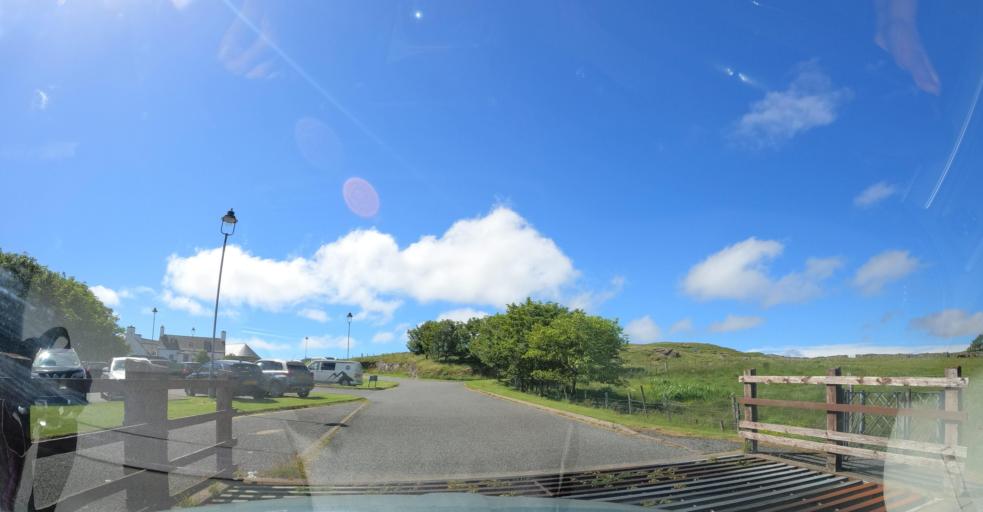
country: GB
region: Scotland
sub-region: Eilean Siar
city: Harris
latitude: 58.1958
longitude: -6.7428
